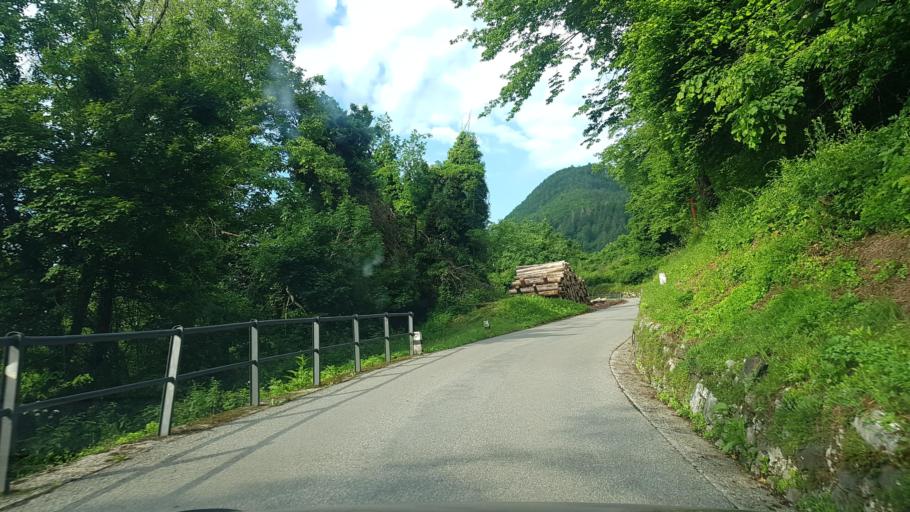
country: IT
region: Friuli Venezia Giulia
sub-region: Provincia di Udine
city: Zuglio
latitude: 46.4673
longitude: 13.0183
